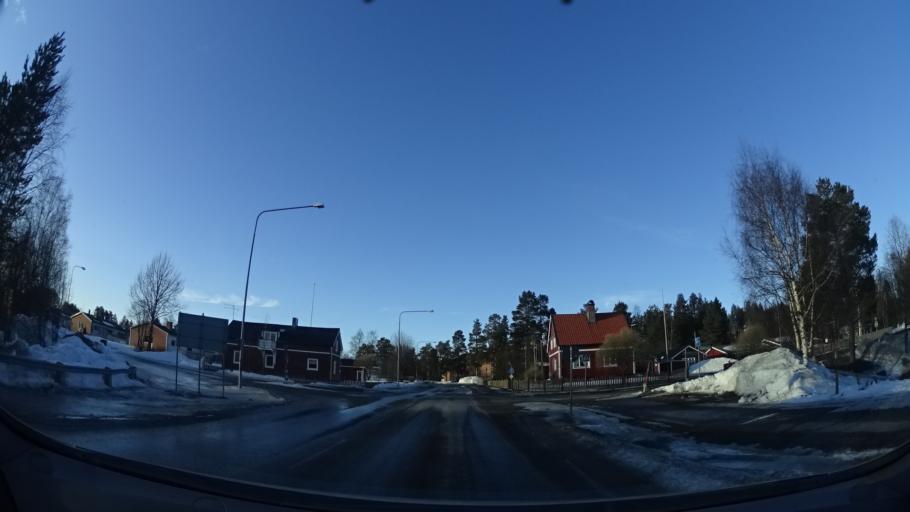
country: SE
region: Vaesterbotten
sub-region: Skelleftea Kommun
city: Byske
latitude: 64.9505
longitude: 21.2182
